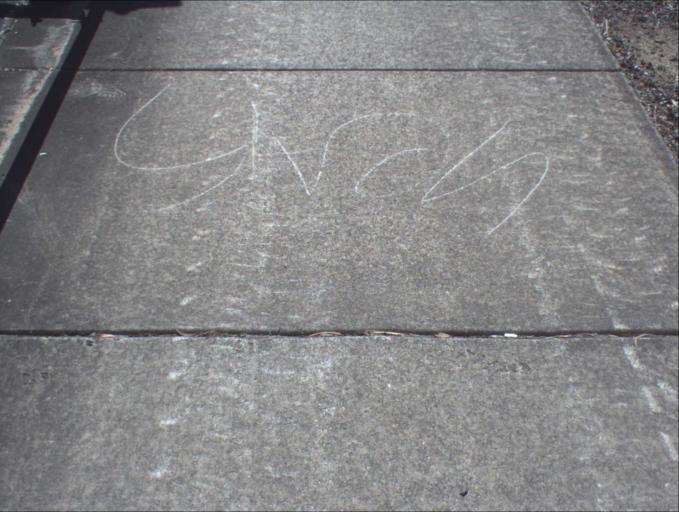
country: AU
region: Queensland
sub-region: Gold Coast
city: Yatala
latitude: -27.7247
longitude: 153.2202
